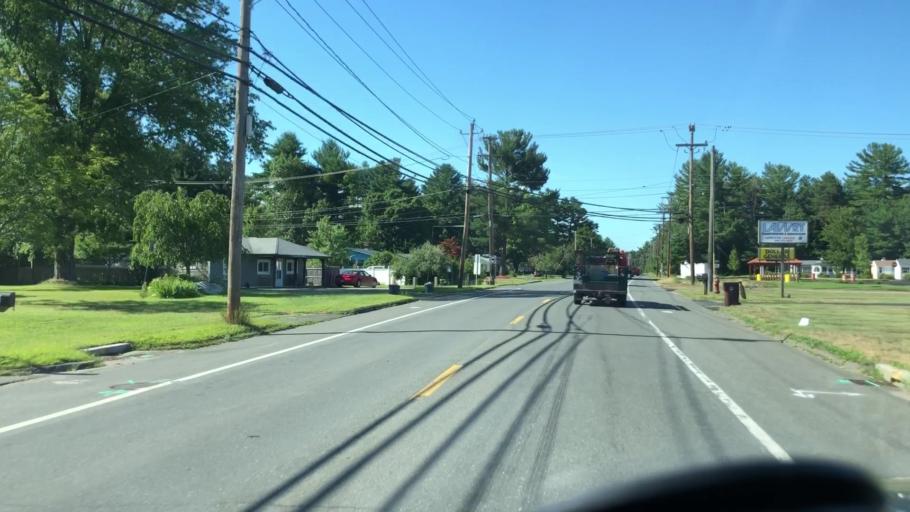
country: US
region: Massachusetts
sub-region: Hampden County
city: Westfield
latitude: 42.1597
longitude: -72.7263
